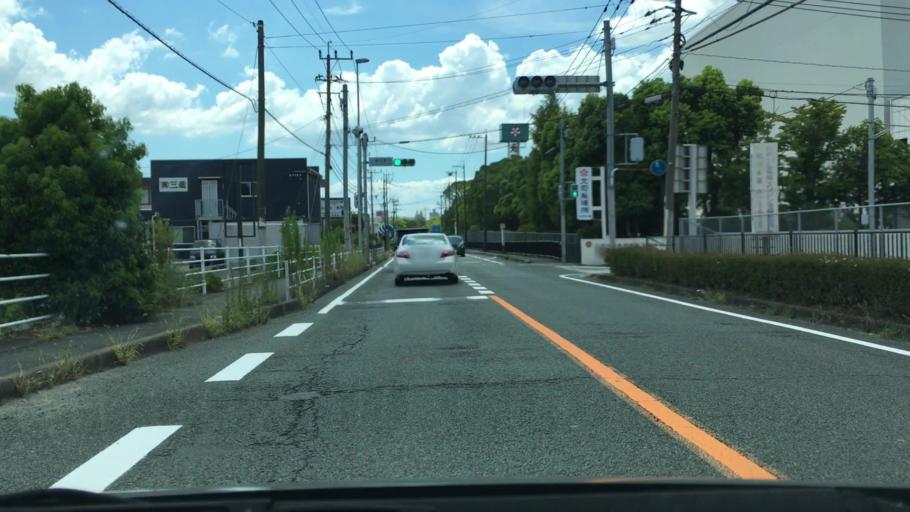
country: JP
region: Saga Prefecture
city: Kanzakimachi-kanzaki
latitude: 33.3394
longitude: 130.4319
